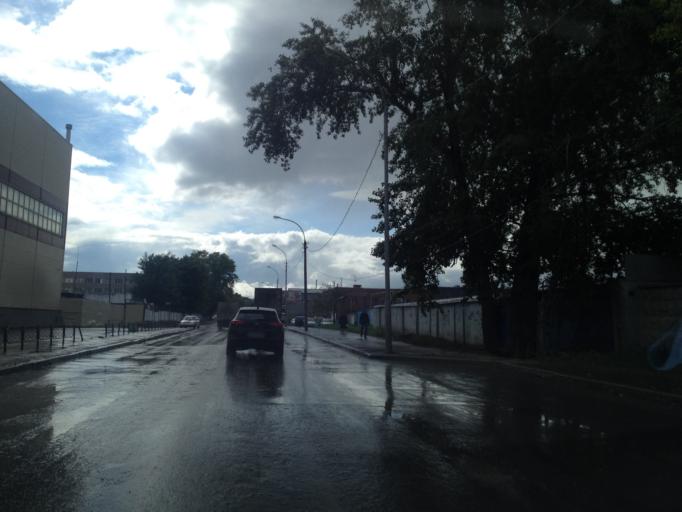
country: RU
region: Sverdlovsk
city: Yekaterinburg
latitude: 56.8669
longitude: 60.5910
